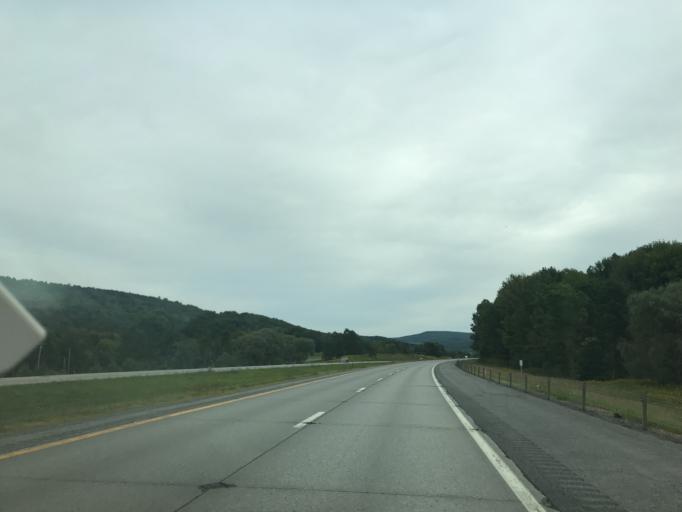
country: US
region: New York
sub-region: Schoharie County
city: Cobleskill
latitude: 42.6483
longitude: -74.5997
